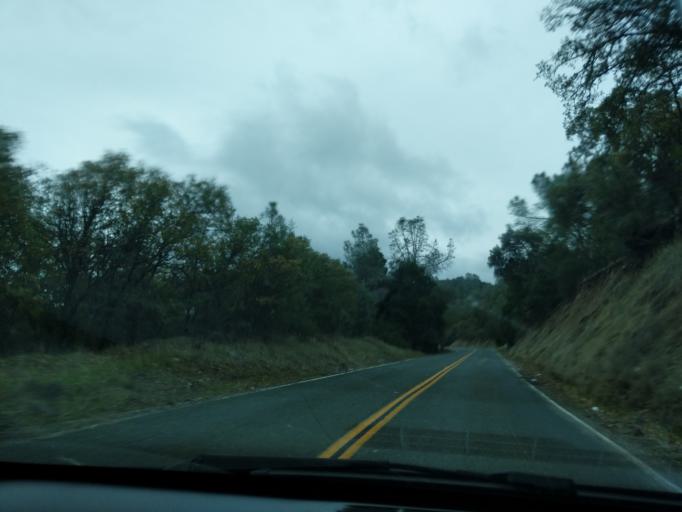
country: US
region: California
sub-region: Monterey County
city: Soledad
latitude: 36.5821
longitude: -121.1923
